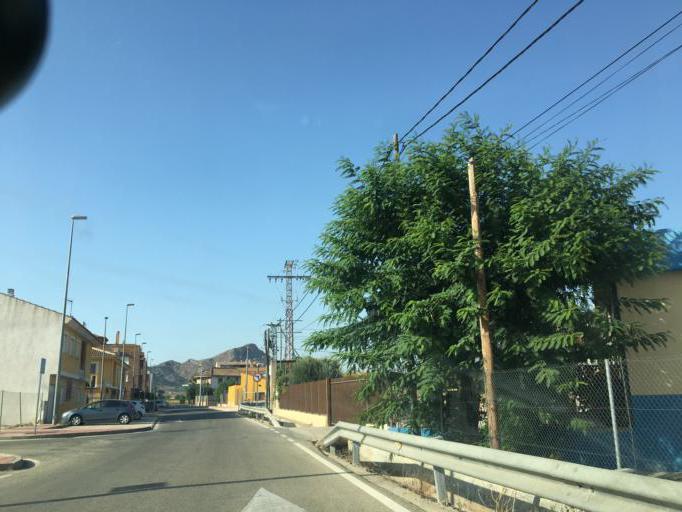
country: ES
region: Murcia
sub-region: Murcia
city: Santomera
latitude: 38.0357
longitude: -1.0749
